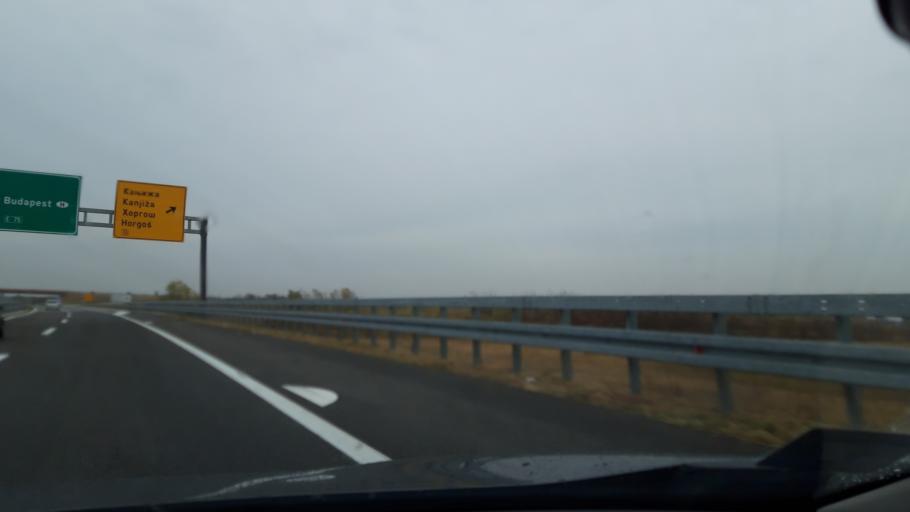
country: HU
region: Csongrad
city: Morahalom
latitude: 46.1503
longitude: 19.9342
